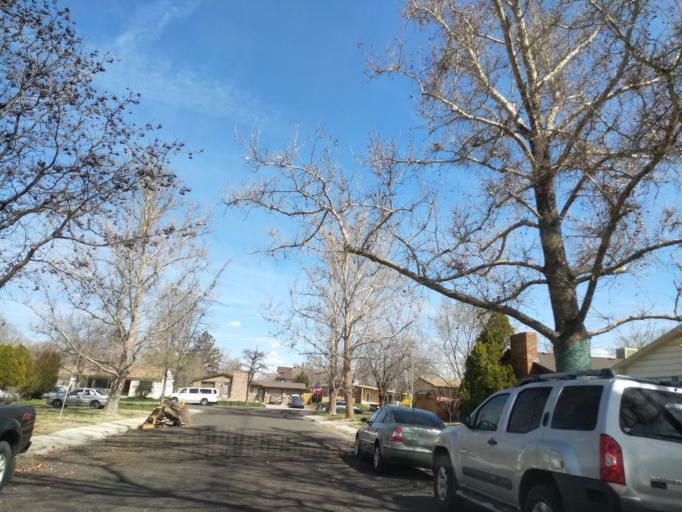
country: US
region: Colorado
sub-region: Mesa County
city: Grand Junction
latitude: 39.0831
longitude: -108.5454
